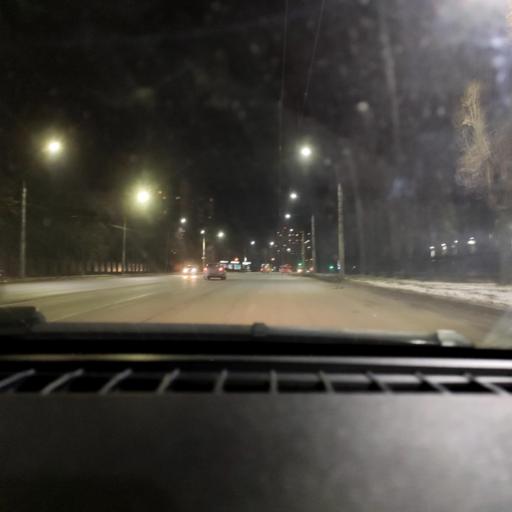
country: RU
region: Voronezj
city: Voronezh
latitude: 51.6789
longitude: 39.2594
